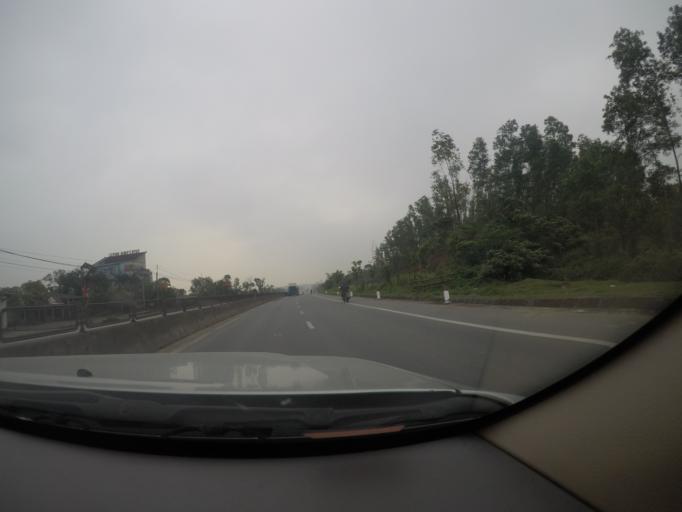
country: VN
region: Ha Tinh
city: Cam Xuyen
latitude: 18.2026
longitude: 106.1545
